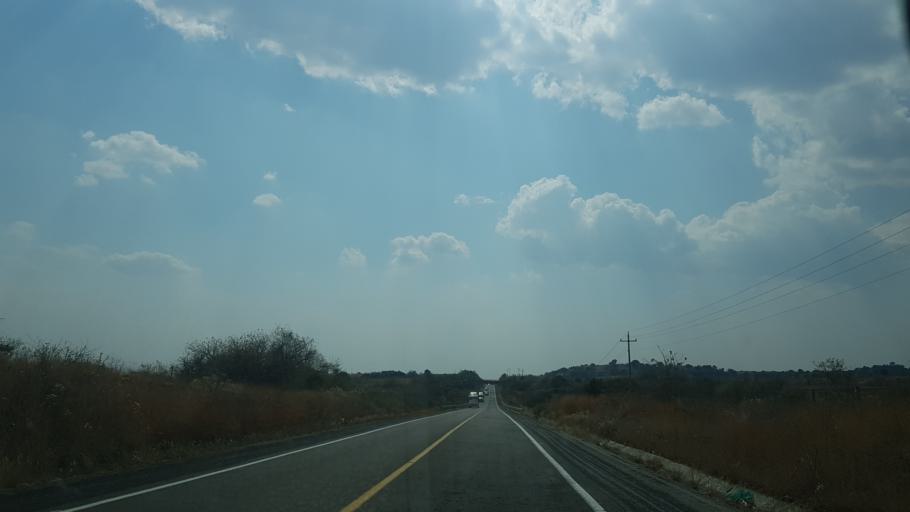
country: MX
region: Puebla
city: San Juan Amecac
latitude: 18.8168
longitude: -98.6586
